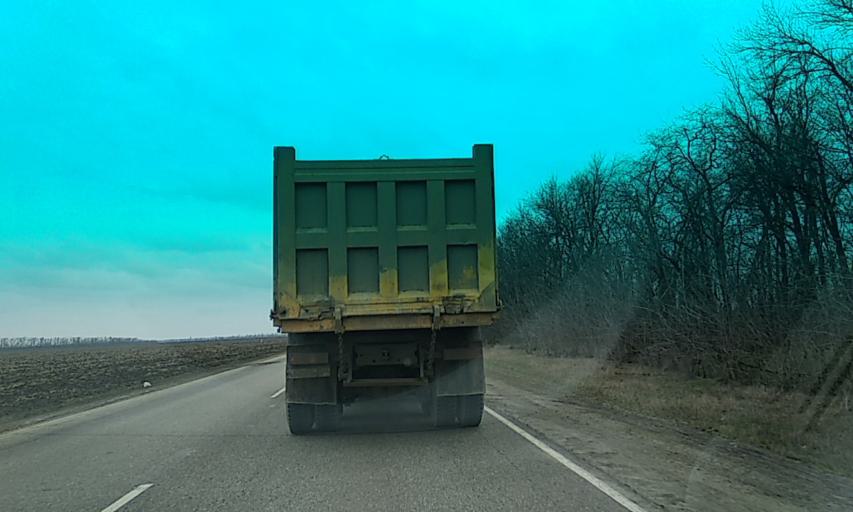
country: RU
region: Krasnodarskiy
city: Vyselki
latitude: 45.5183
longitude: 39.7053
